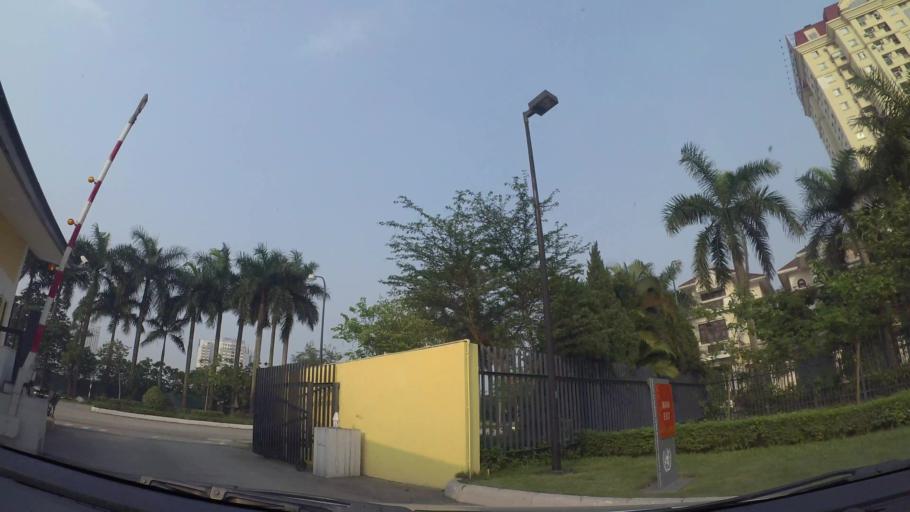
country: VN
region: Ha Noi
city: Tay Ho
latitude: 21.0753
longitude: 105.8095
